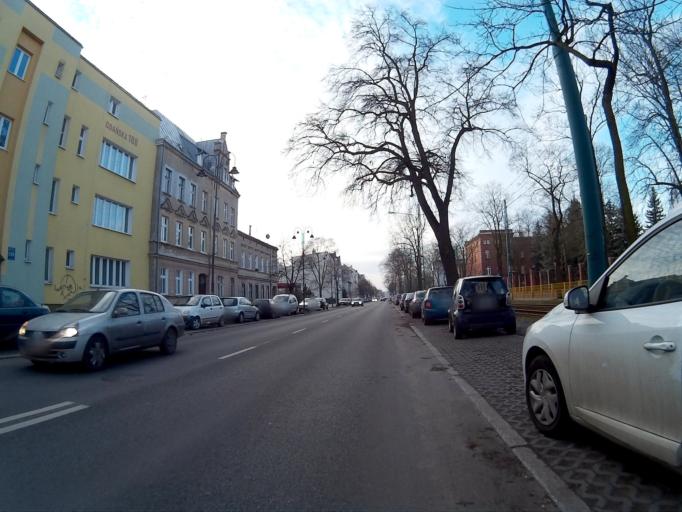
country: PL
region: Kujawsko-Pomorskie
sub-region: Bydgoszcz
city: Bydgoszcz
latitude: 53.1406
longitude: 18.0185
